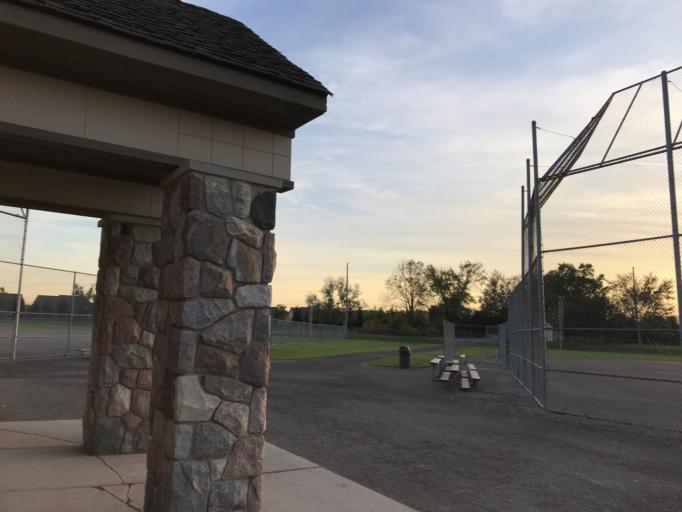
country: US
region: Michigan
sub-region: Oakland County
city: Farmington
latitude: 42.4413
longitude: -83.4027
